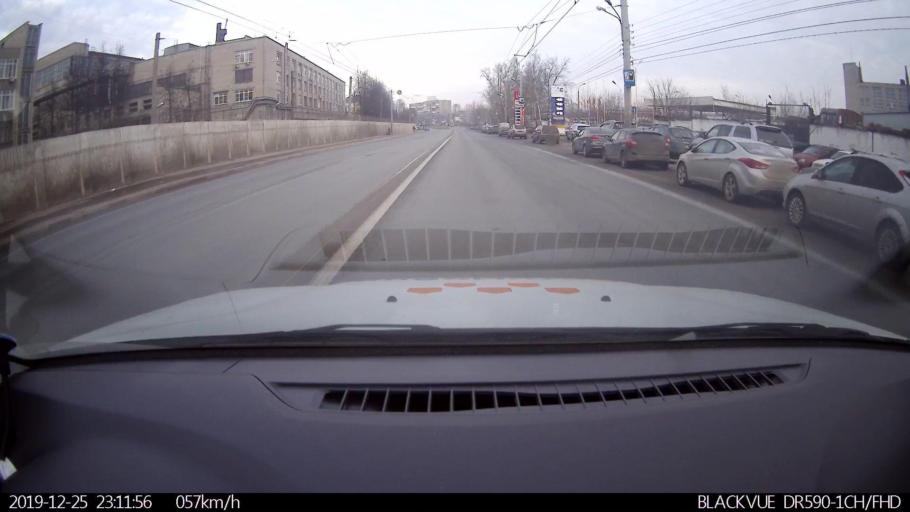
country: RU
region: Nizjnij Novgorod
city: Nizhniy Novgorod
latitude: 56.3216
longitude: 43.9091
